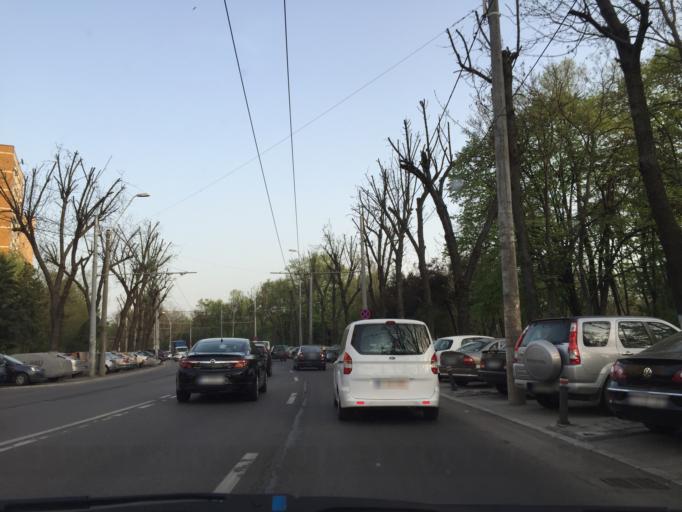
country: RO
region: Bucuresti
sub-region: Municipiul Bucuresti
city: Bucuresti
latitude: 44.4128
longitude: 26.1056
